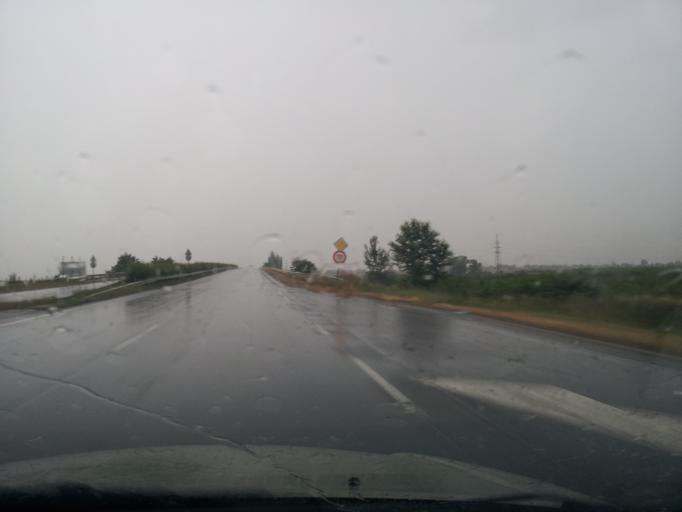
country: HU
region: Borsod-Abauj-Zemplen
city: Onga
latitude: 48.1059
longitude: 20.9050
